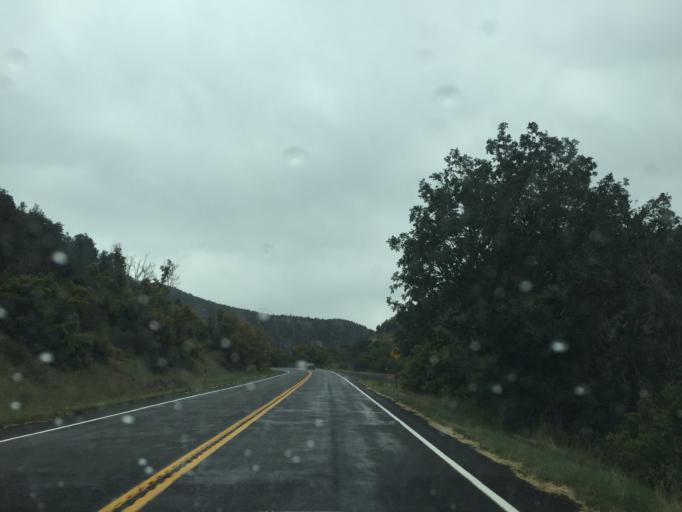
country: US
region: Utah
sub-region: Kane County
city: Kanab
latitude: 37.3518
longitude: -112.5981
